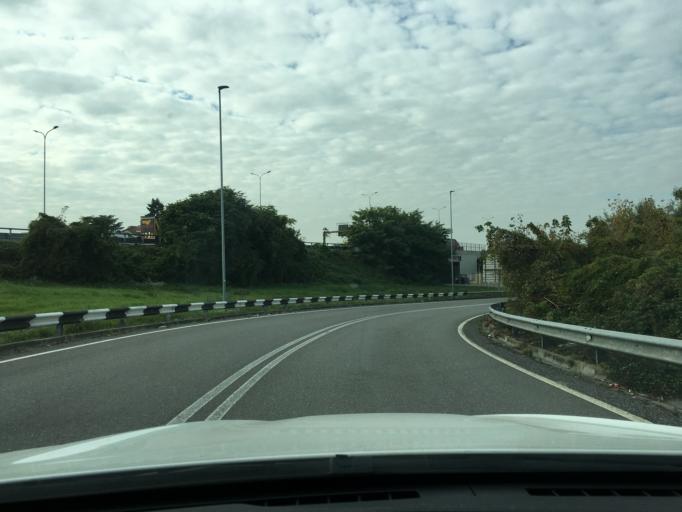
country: IT
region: Lombardy
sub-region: Provincia di Monza e Brianza
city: Muggio
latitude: 45.5905
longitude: 9.2474
